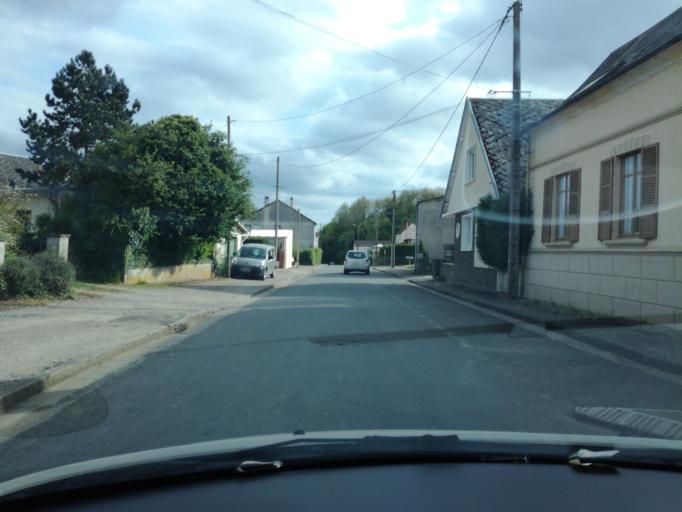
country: FR
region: Picardie
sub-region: Departement de la Somme
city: Poix-de-Picardie
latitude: 49.7890
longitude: 1.9907
